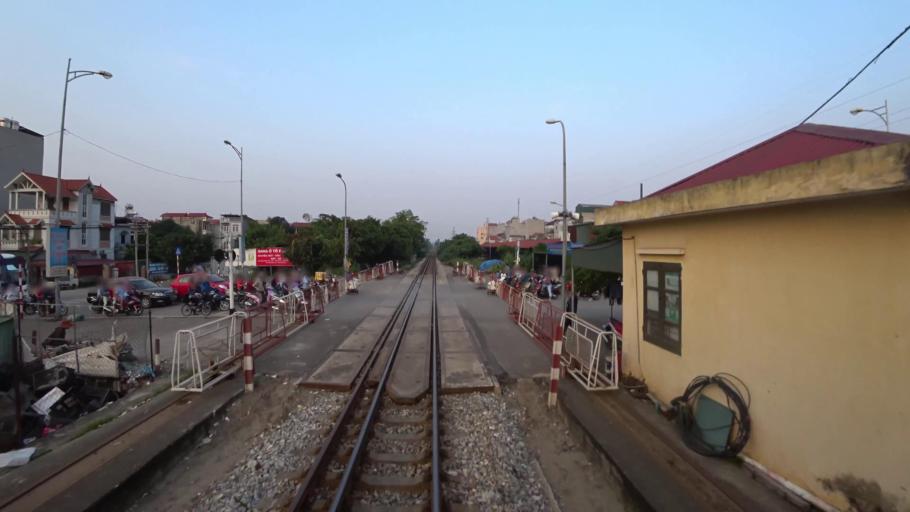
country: VN
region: Ha Noi
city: Trau Quy
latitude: 21.0859
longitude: 105.9163
